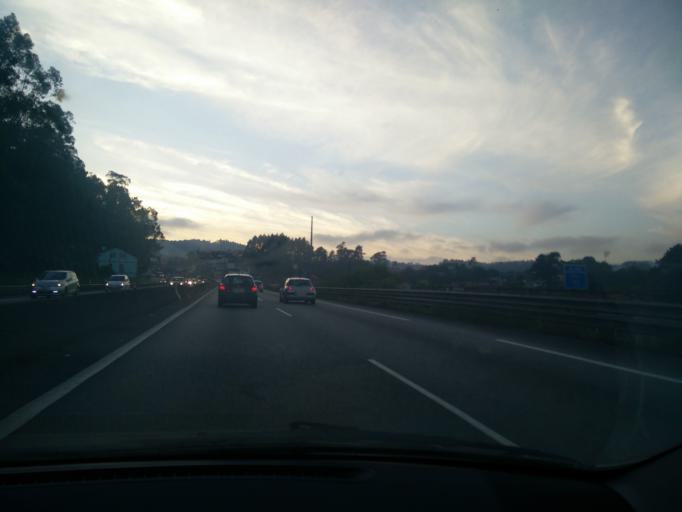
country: ES
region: Galicia
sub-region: Provincia de Pontevedra
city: Porrino
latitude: 42.1928
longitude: -8.6415
